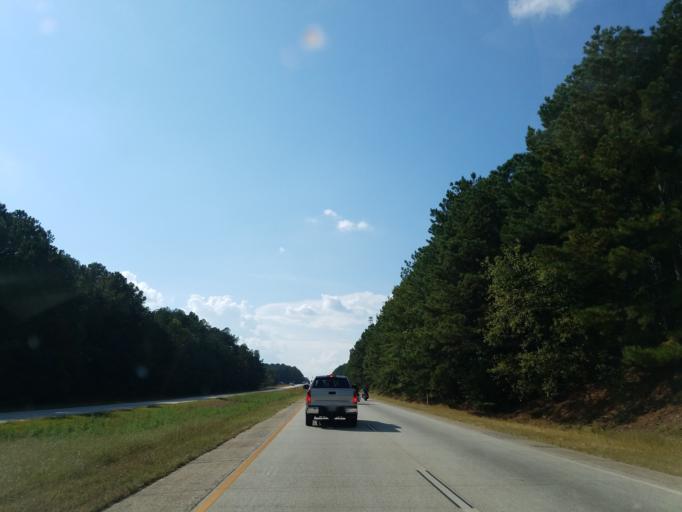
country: US
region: Georgia
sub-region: Barrow County
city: Auburn
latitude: 33.9603
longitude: -83.7909
